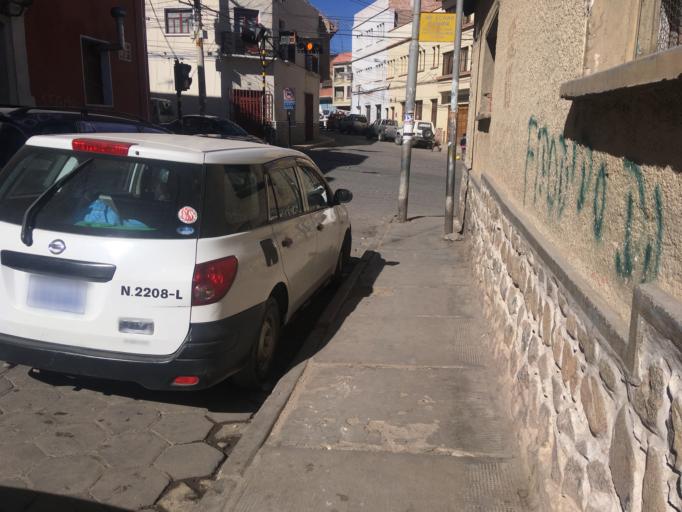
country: BO
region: Potosi
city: Potosi
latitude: -19.5843
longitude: -65.7550
